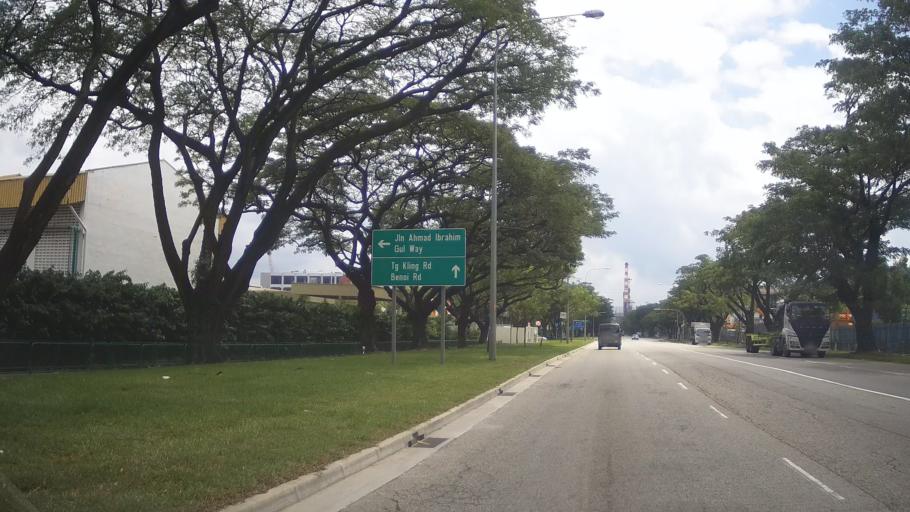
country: MY
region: Johor
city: Johor Bahru
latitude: 1.3086
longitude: 103.6695
